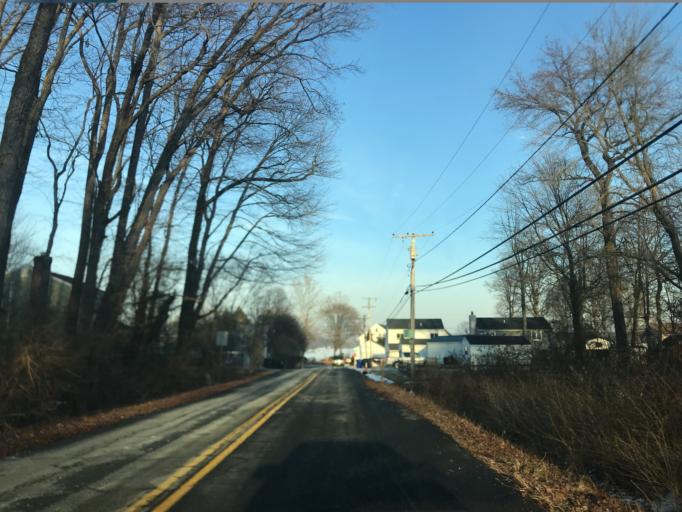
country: US
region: Maryland
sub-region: Harford County
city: Riverside
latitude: 39.4365
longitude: -76.2518
